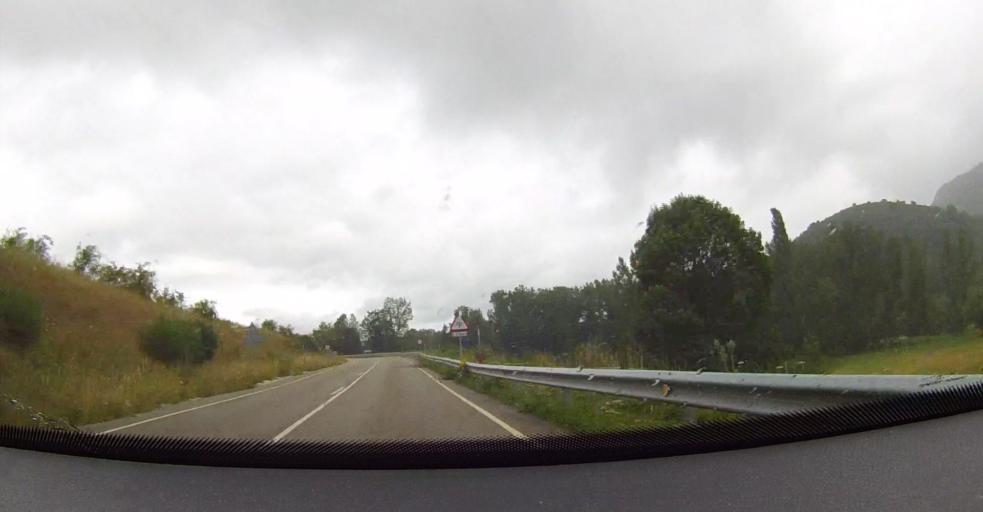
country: ES
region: Castille and Leon
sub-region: Provincia de Leon
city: Acebedo
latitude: 43.0385
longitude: -5.0978
